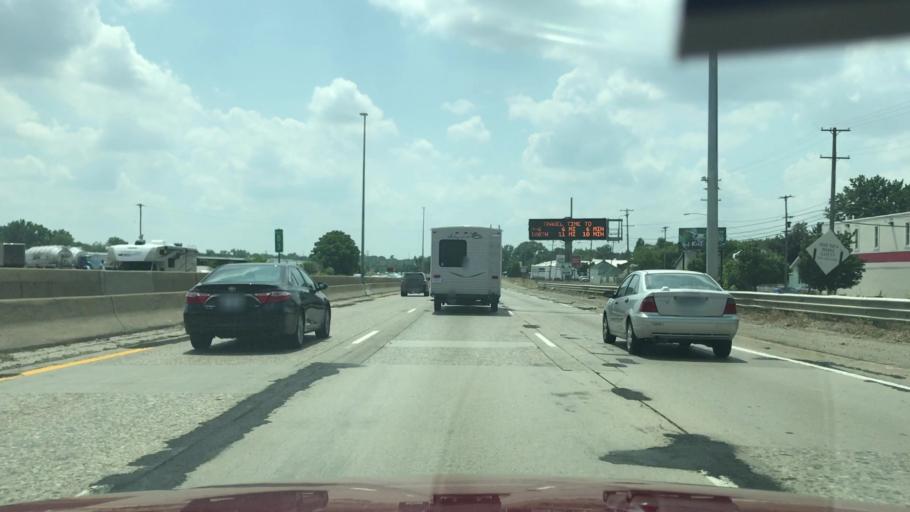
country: US
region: Michigan
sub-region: Kent County
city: Grand Rapids
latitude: 42.9376
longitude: -85.6796
